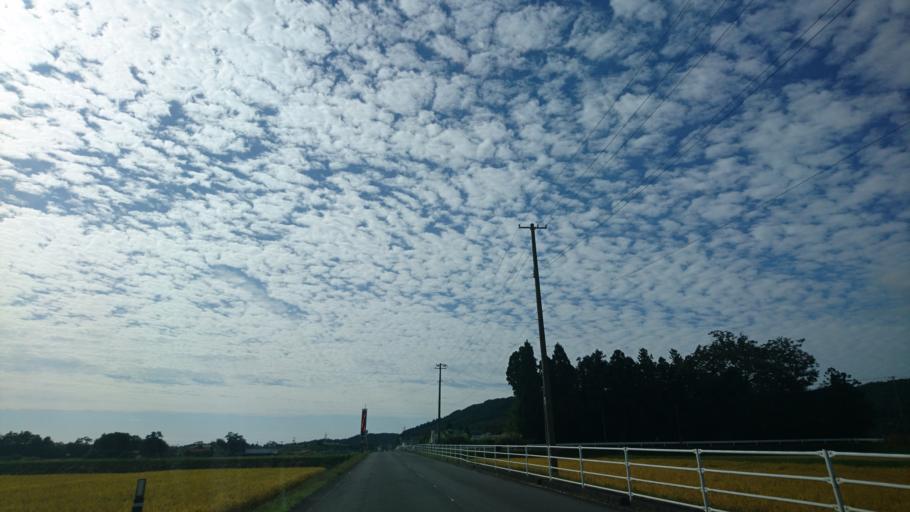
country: JP
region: Fukushima
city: Sukagawa
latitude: 37.3240
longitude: 140.2671
